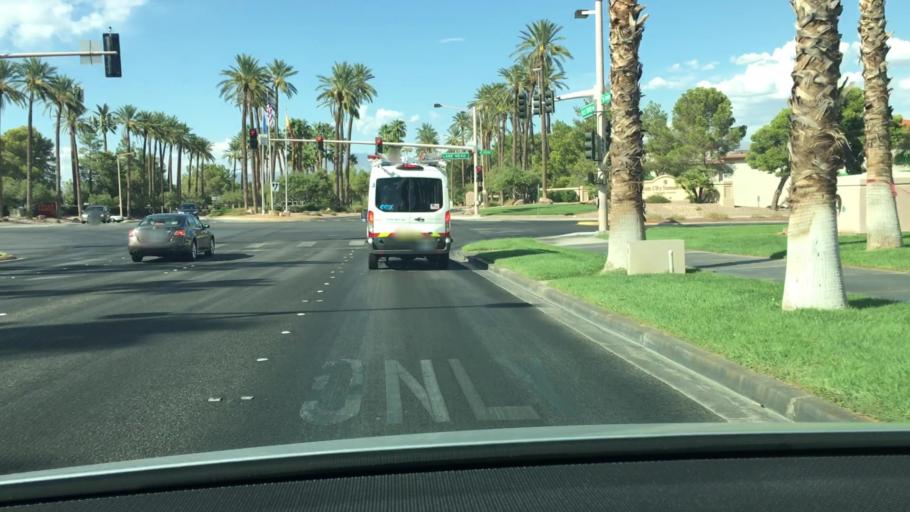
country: US
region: Nevada
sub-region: Clark County
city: Summerlin South
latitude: 36.2056
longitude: -115.2998
